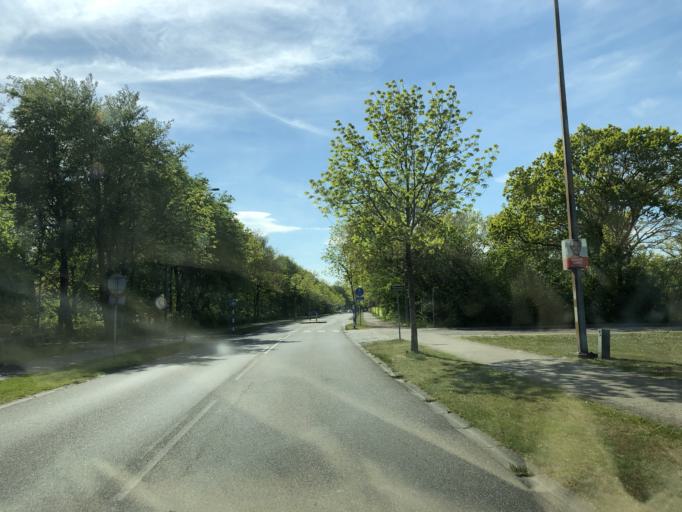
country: DK
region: Central Jutland
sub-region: Ringkobing-Skjern Kommune
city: Skjern
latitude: 55.9428
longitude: 8.5064
